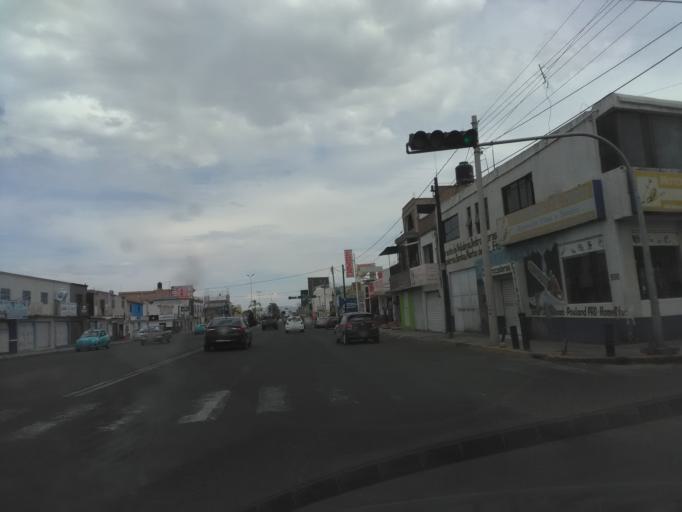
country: MX
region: Durango
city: Victoria de Durango
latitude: 24.0188
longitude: -104.6574
